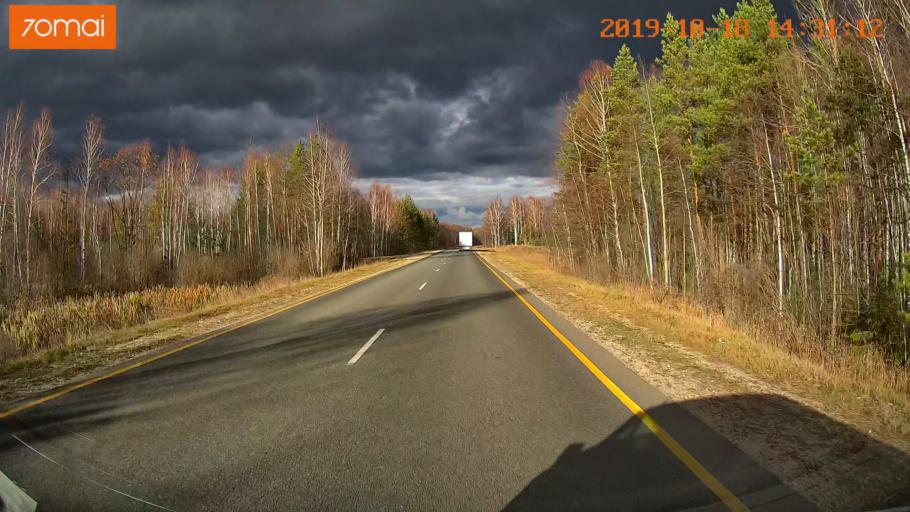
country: RU
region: Rjazan
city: Tuma
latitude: 55.1794
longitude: 40.5688
